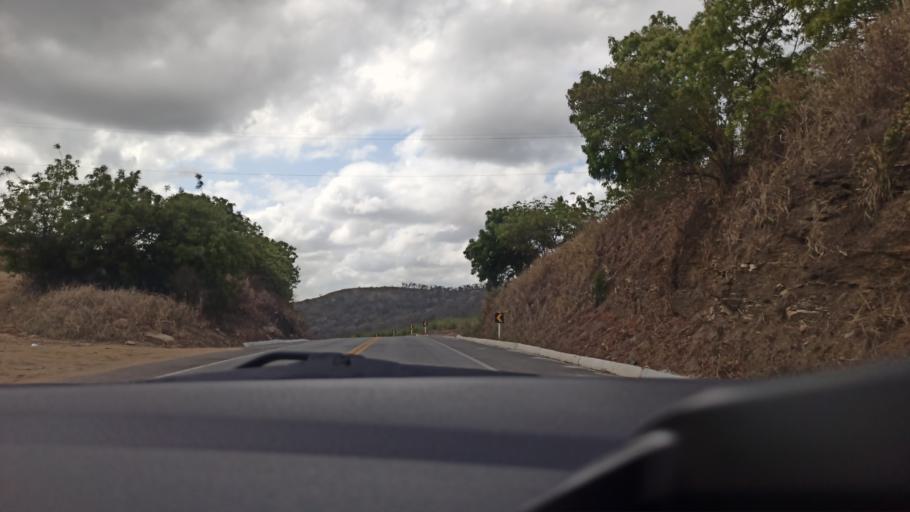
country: BR
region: Pernambuco
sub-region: Timbauba
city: Timbauba
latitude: -7.5346
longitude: -35.2883
